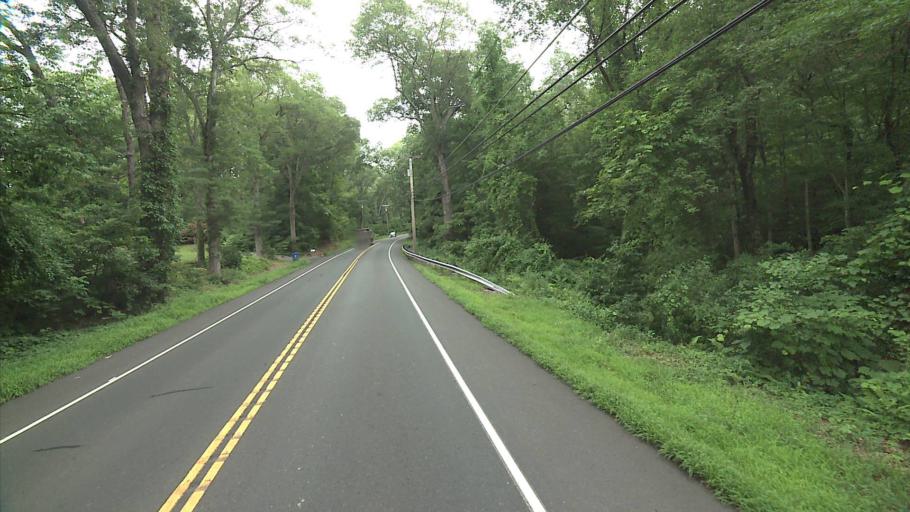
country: US
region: Connecticut
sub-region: Tolland County
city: Tolland
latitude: 41.8852
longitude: -72.3351
